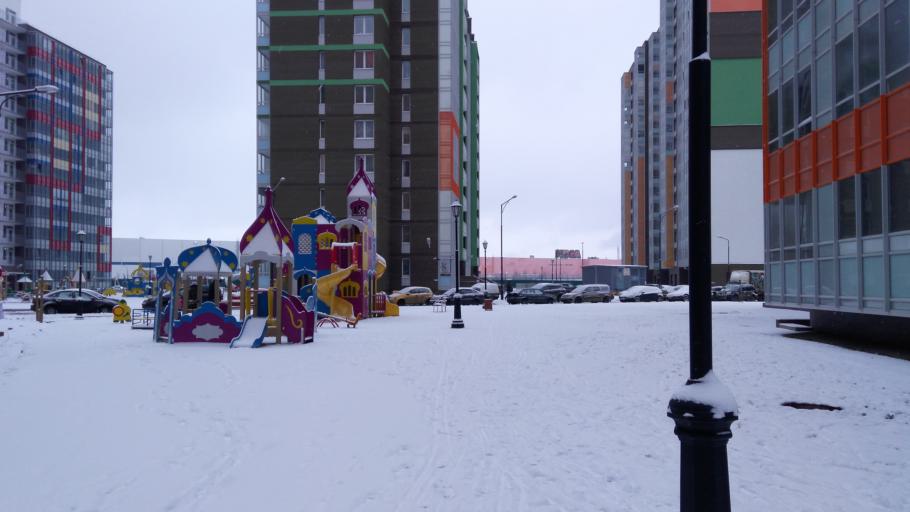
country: RU
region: Leningrad
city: Rybatskoye
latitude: 59.8989
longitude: 30.5149
